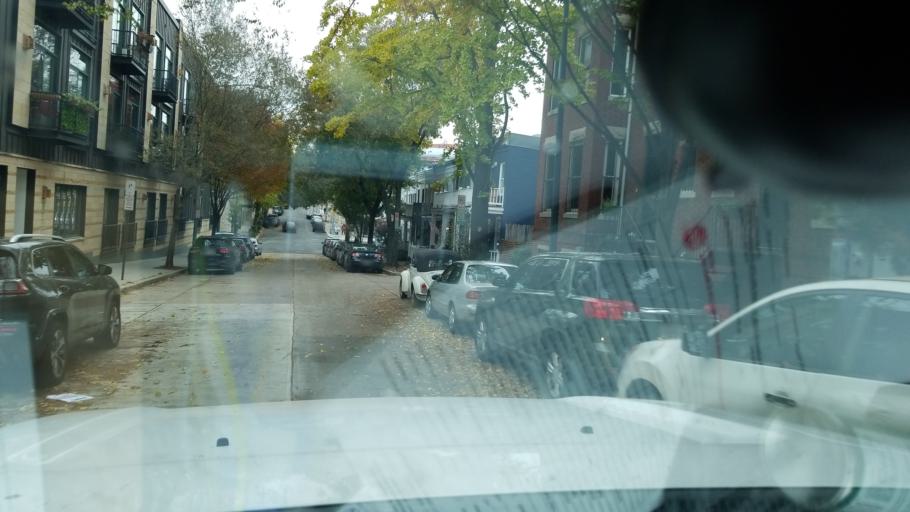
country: US
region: Washington, D.C.
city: Washington, D.C.
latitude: 38.9206
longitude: -77.0389
